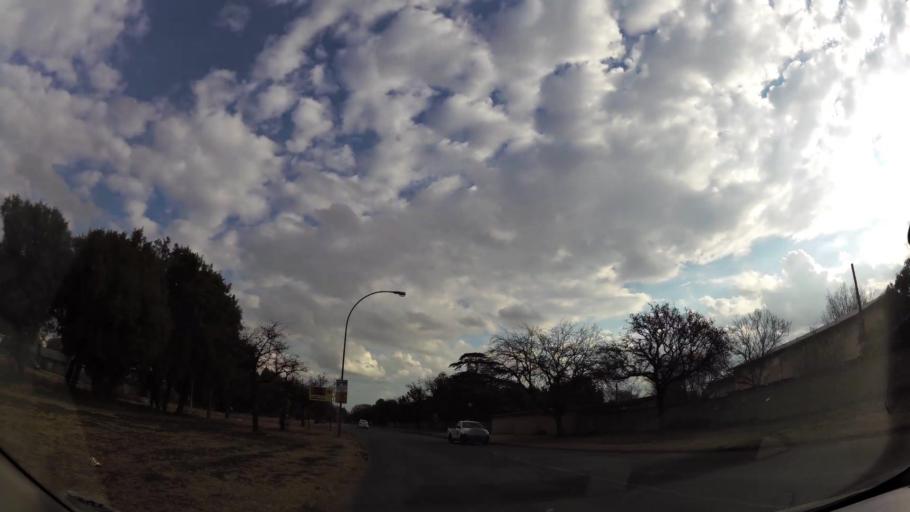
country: ZA
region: Orange Free State
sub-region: Fezile Dabi District Municipality
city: Sasolburg
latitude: -26.8222
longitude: 27.8331
